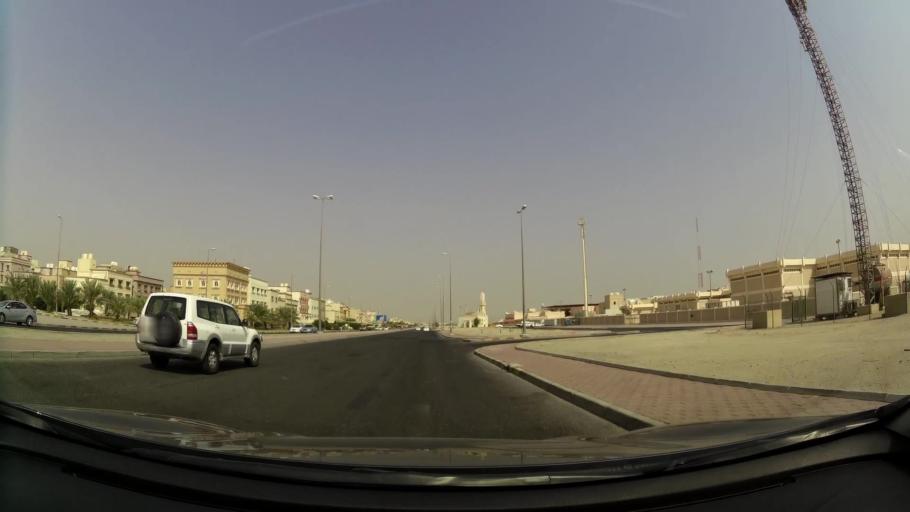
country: KW
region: Muhafazat al Jahra'
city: Al Jahra'
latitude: 29.2988
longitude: 47.7230
